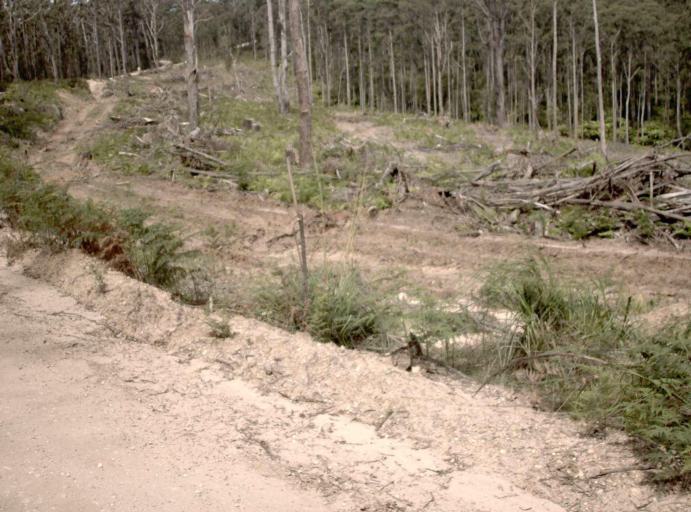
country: AU
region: Victoria
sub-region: East Gippsland
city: Lakes Entrance
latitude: -37.6367
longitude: 148.6648
